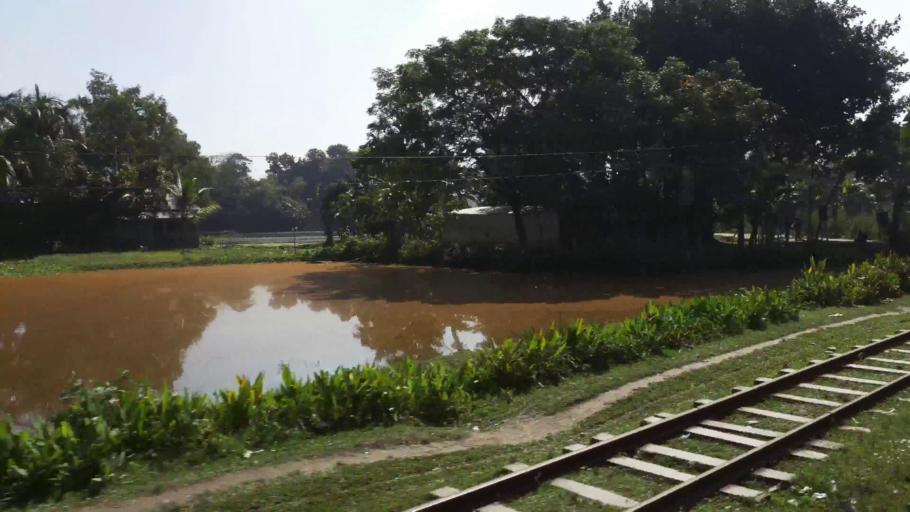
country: BD
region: Dhaka
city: Gafargaon
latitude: 24.4972
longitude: 90.5225
